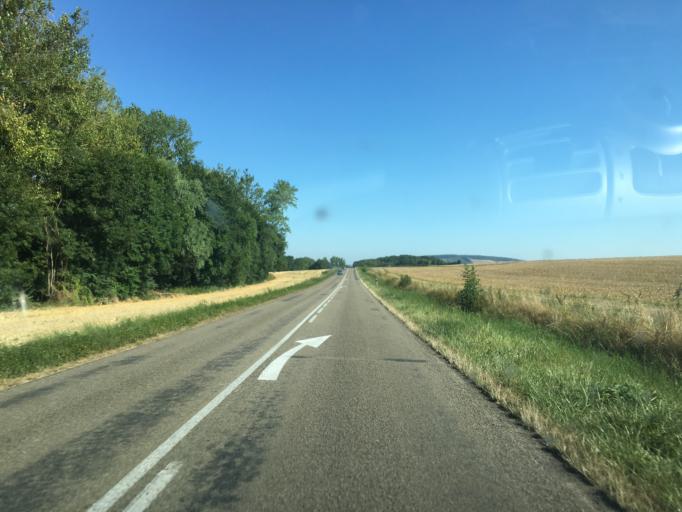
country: FR
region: Bourgogne
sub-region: Departement de l'Yonne
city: Aillant-sur-Tholon
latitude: 47.8944
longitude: 3.3547
